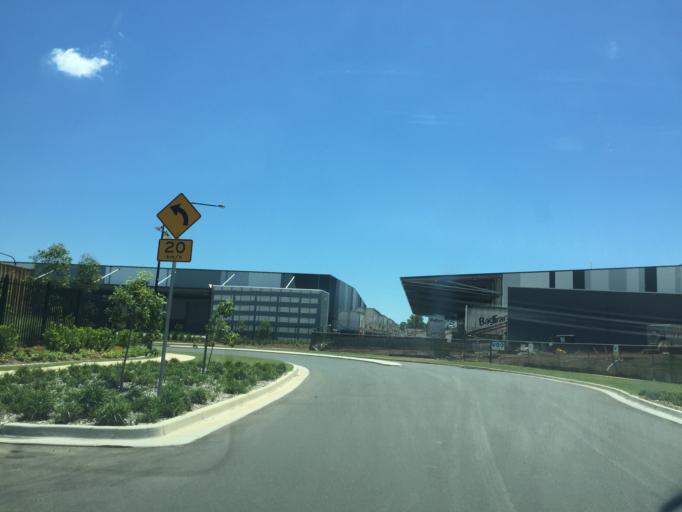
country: AU
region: New South Wales
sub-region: Blacktown
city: Doonside
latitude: -33.7943
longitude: 150.8686
